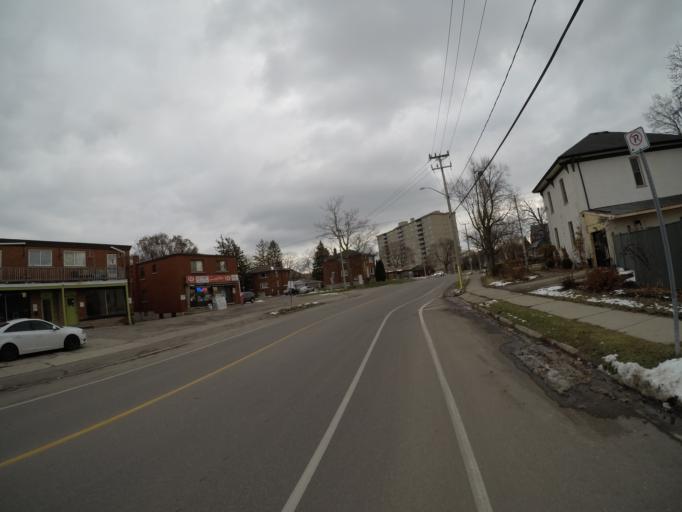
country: CA
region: Ontario
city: Waterloo
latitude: 43.4627
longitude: -80.4938
